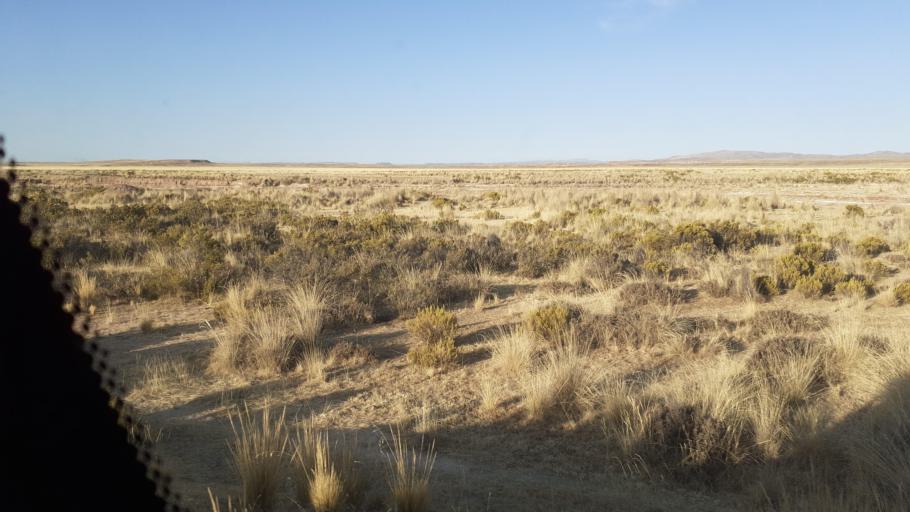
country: BO
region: La Paz
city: Tiahuanaco
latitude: -16.9416
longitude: -68.7636
